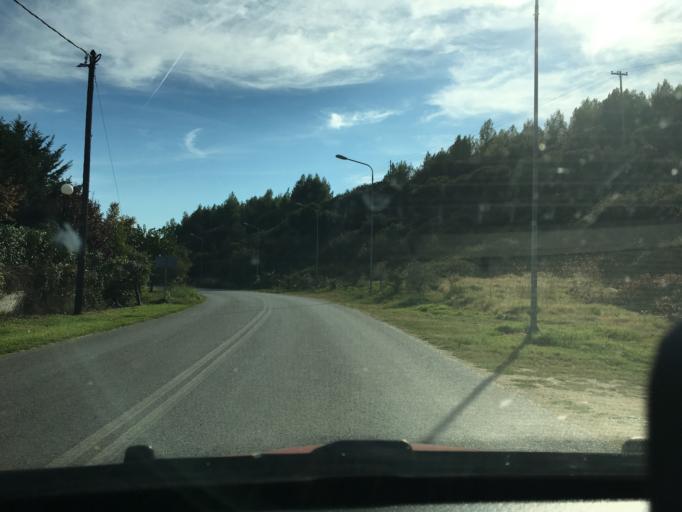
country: GR
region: Central Macedonia
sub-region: Nomos Chalkidikis
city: Agios Nikolaos
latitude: 40.3121
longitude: 23.6958
